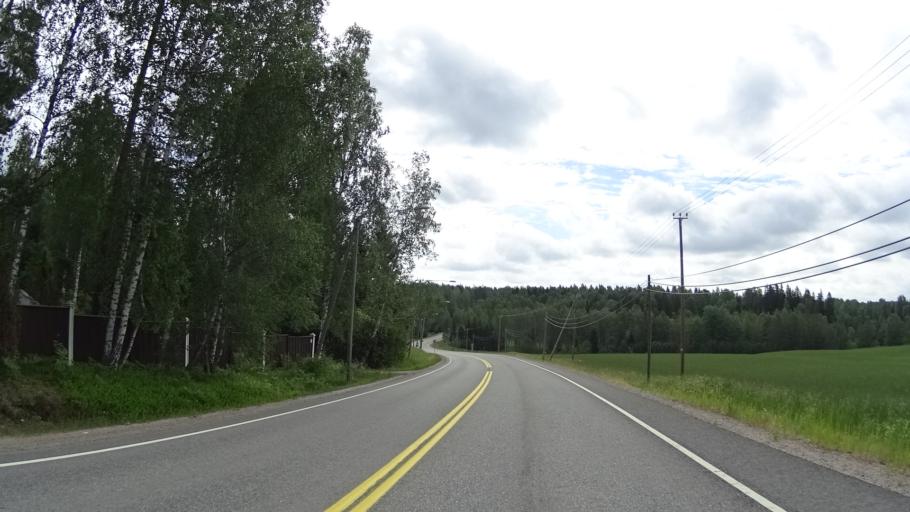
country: FI
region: Uusimaa
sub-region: Helsinki
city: Vihti
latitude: 60.2938
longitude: 24.3950
